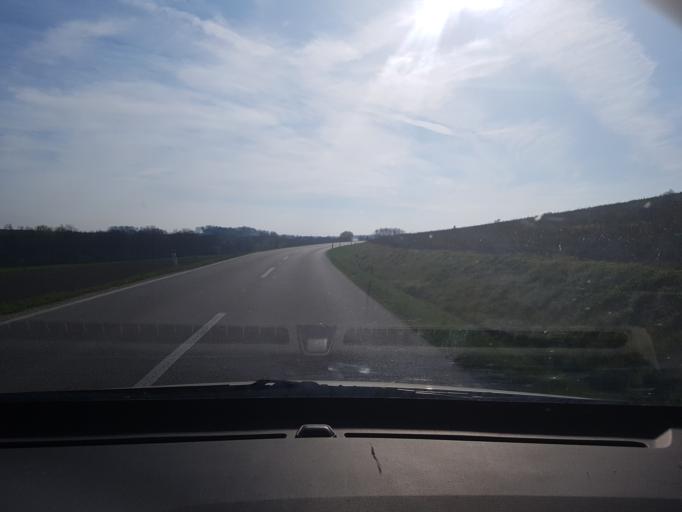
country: AT
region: Upper Austria
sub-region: Politischer Bezirk Linz-Land
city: Sankt Florian
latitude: 48.1904
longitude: 14.3382
